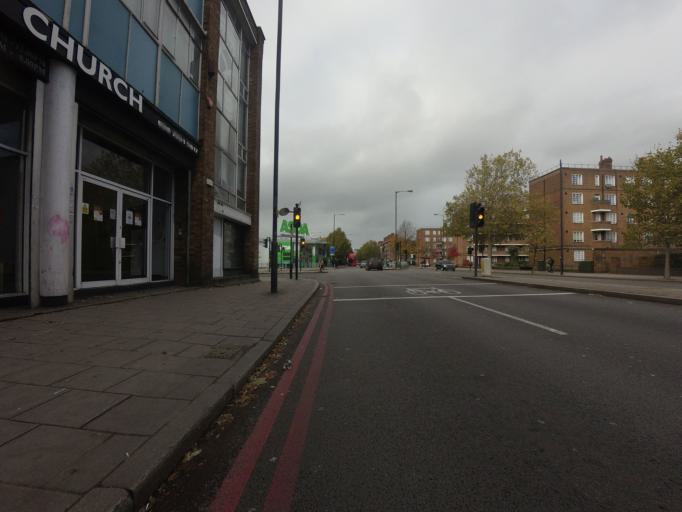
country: GB
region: England
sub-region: Greater London
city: Camberwell
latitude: 51.4850
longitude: -0.0688
